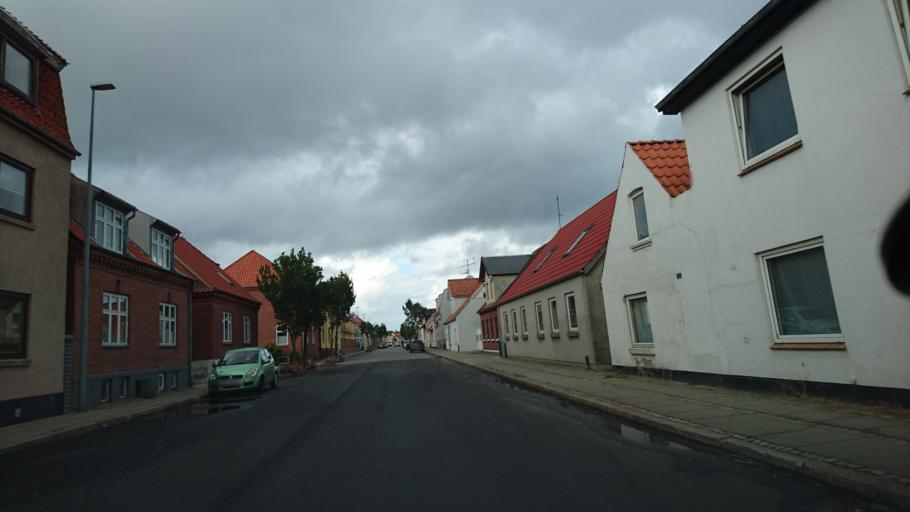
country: DK
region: North Denmark
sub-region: Frederikshavn Kommune
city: Frederikshavn
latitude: 57.4302
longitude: 10.5238
